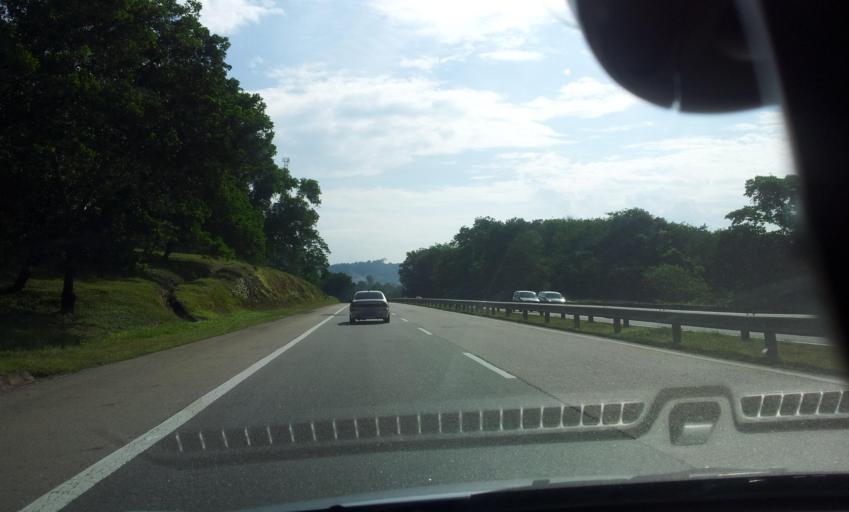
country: MY
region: Pahang
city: Mentekab
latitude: 3.5195
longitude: 102.1597
